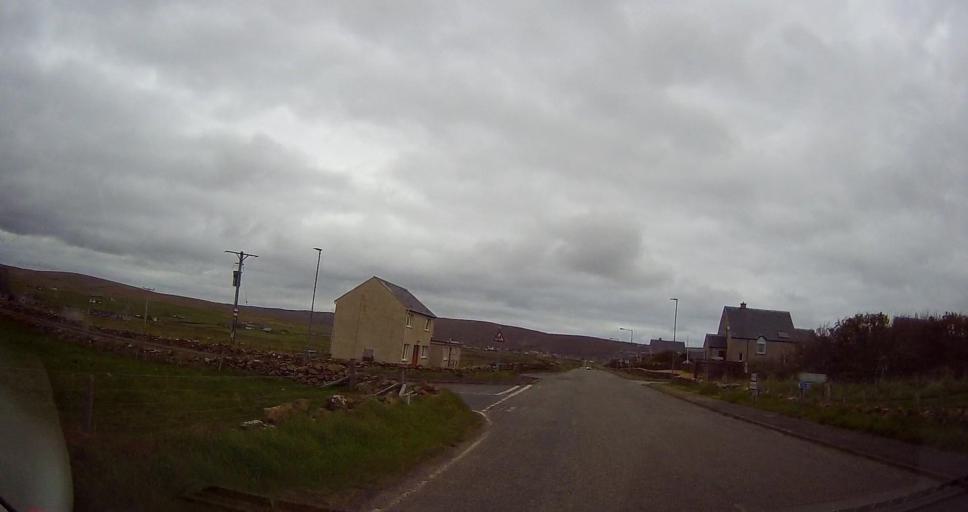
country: GB
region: Scotland
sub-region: Shetland Islands
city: Shetland
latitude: 60.7630
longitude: -0.8583
